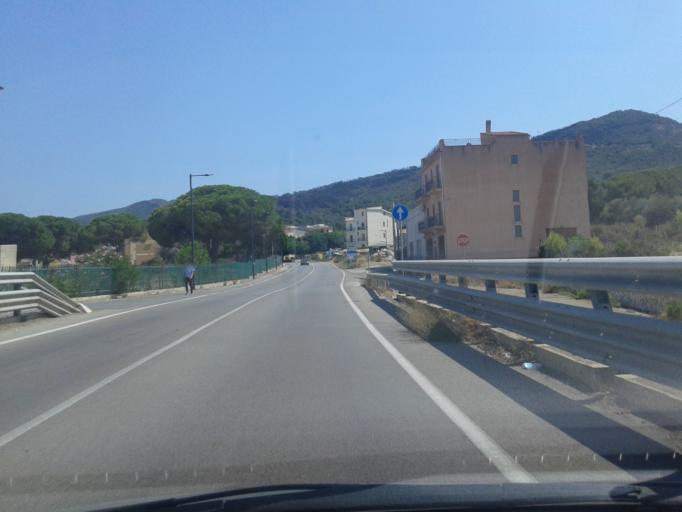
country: IT
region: Sicily
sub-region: Palermo
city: Finale
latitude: 38.0217
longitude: 14.1571
